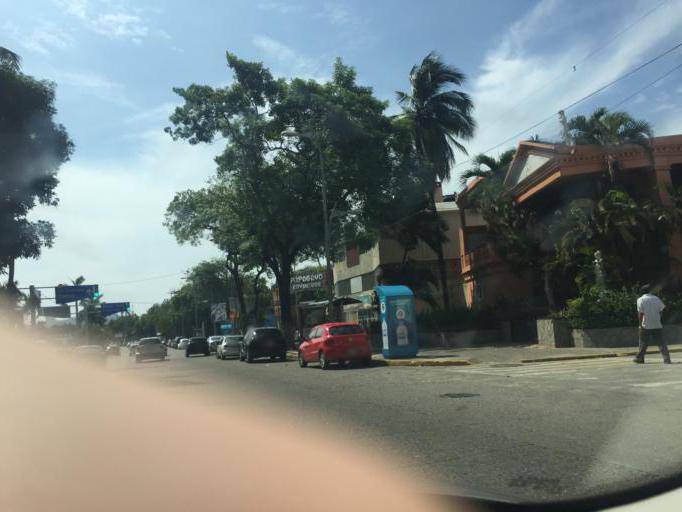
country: MX
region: Guerrero
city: Acapulco de Juarez
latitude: 16.8605
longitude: -99.8835
